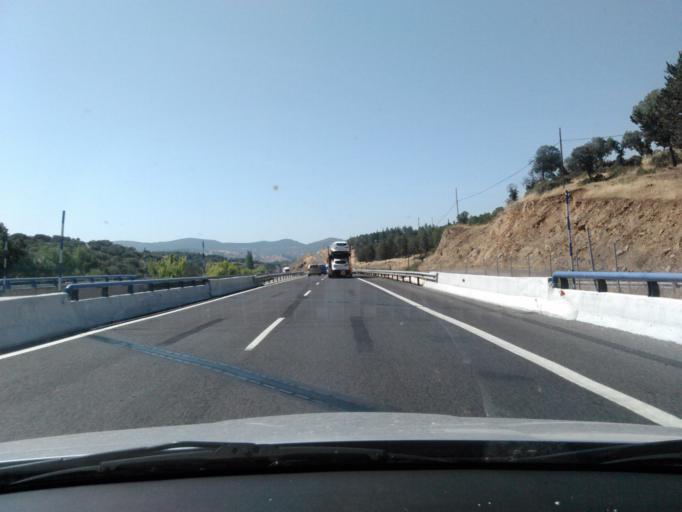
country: ES
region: Castille-La Mancha
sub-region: Provincia de Ciudad Real
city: Viso del Marques
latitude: 38.4482
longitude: -3.4971
